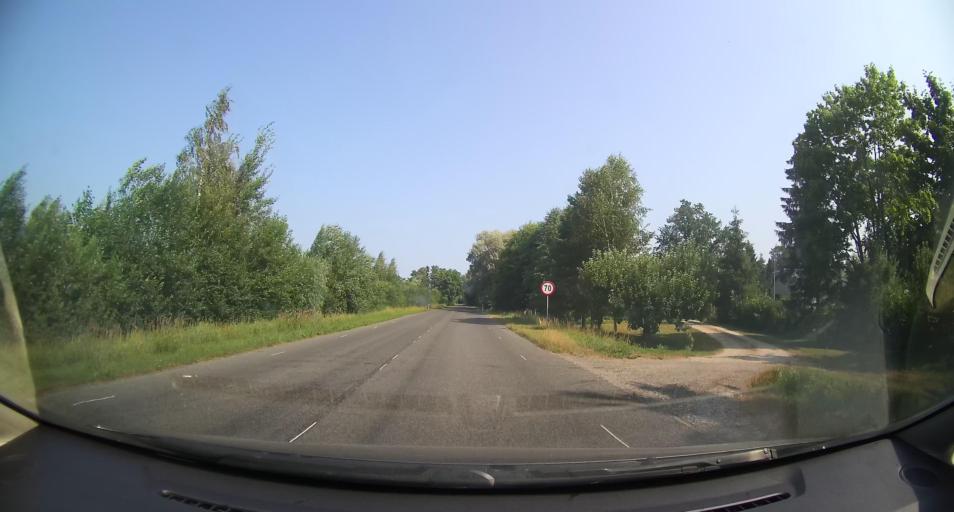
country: EE
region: Paernumaa
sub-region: Audru vald
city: Audru
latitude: 58.4892
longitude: 24.3357
